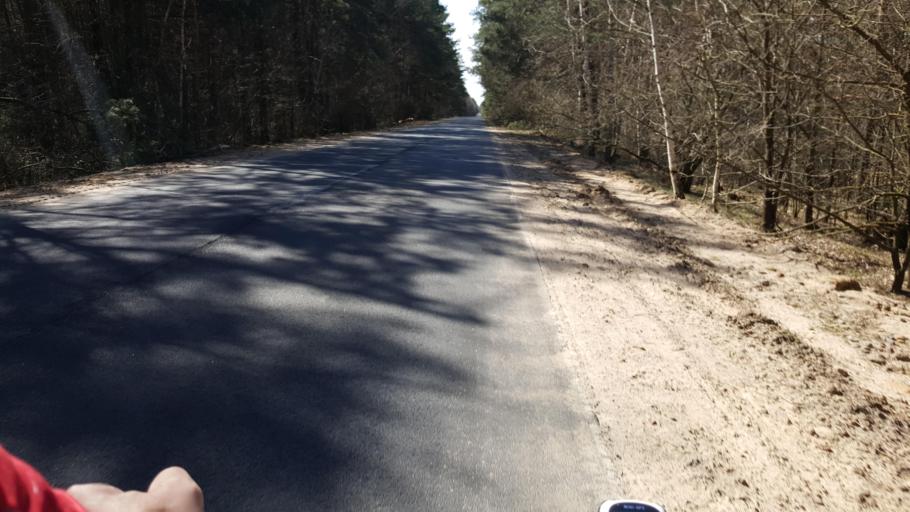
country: BY
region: Brest
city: Charnawchytsy
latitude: 52.2916
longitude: 23.8083
